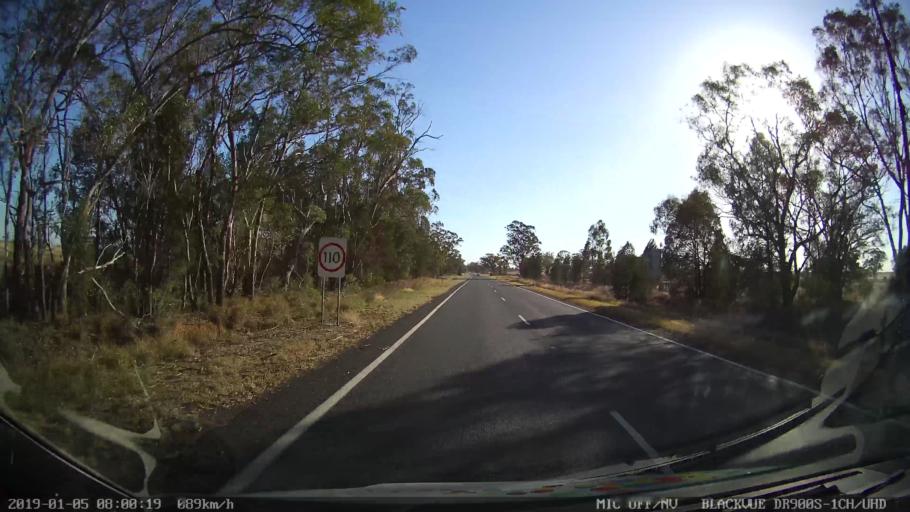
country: AU
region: New South Wales
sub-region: Gilgandra
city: Gilgandra
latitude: -31.6941
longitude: 148.6867
